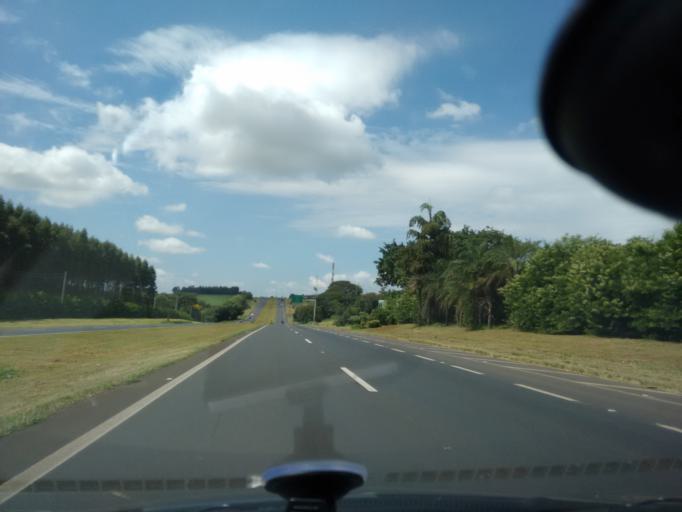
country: BR
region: Sao Paulo
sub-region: Ibate
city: Ibate
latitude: -21.9455
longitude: -48.0000
